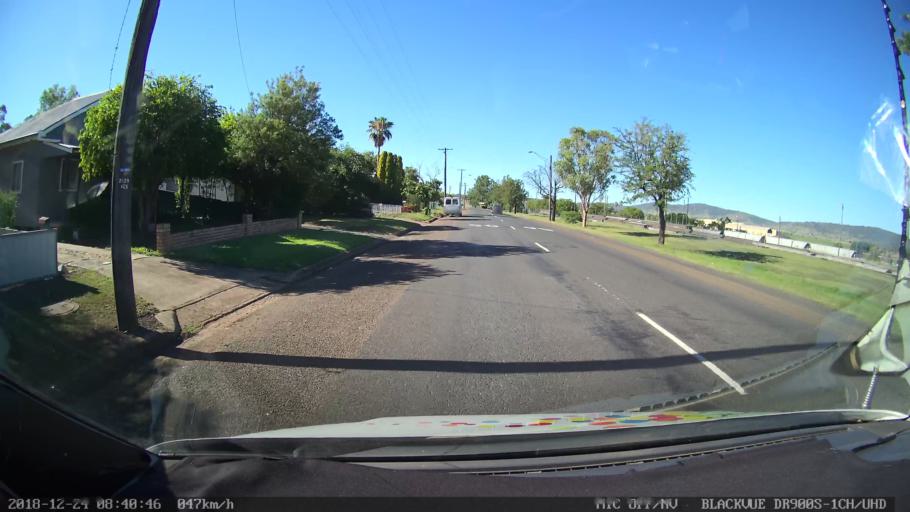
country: AU
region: New South Wales
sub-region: Liverpool Plains
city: Quirindi
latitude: -31.3573
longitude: 150.6460
